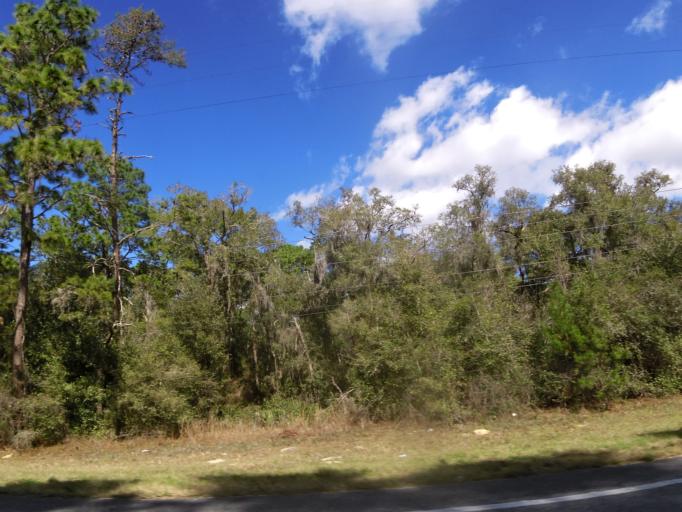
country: US
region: Florida
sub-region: Volusia County
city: De Leon Springs
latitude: 29.1382
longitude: -81.3562
